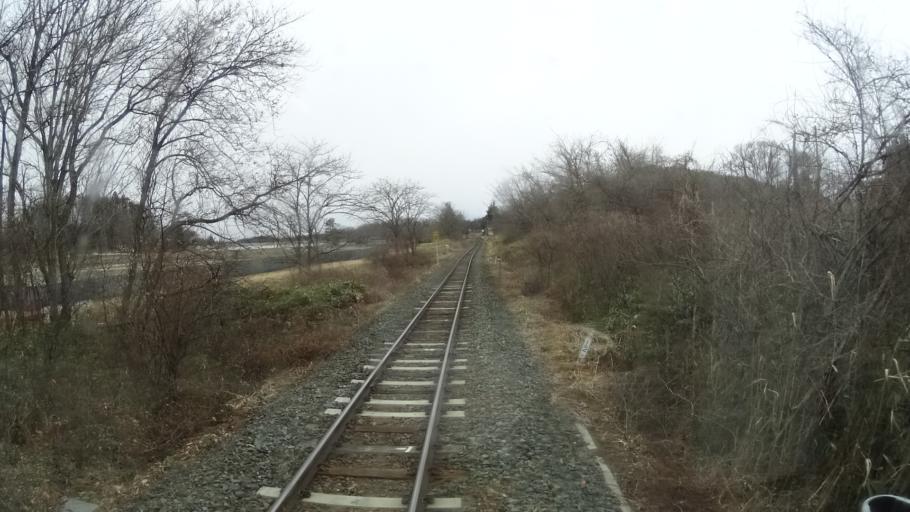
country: JP
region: Iwate
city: Hanamaki
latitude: 39.4075
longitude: 141.1964
